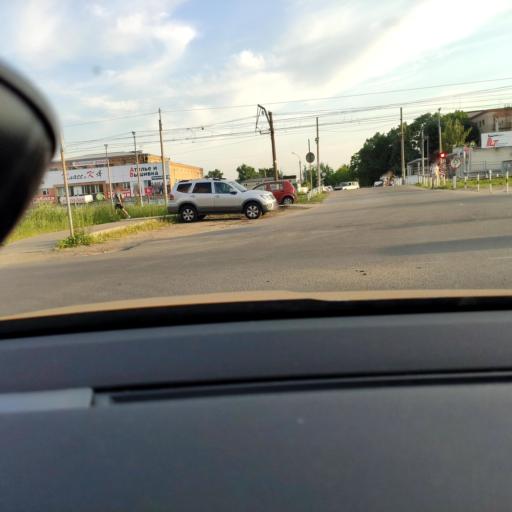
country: RU
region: Moskovskaya
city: Shchelkovo
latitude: 55.9182
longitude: 37.9784
